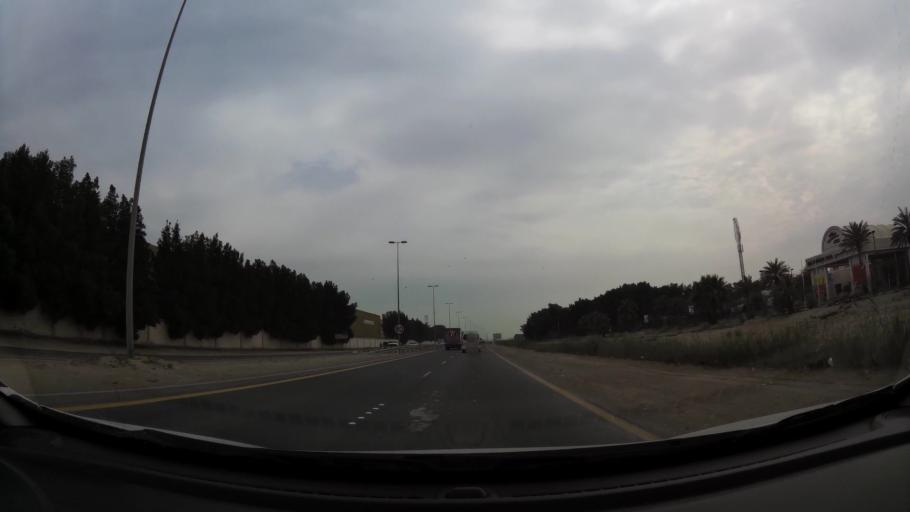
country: BH
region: Northern
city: Sitrah
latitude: 26.0841
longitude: 50.6123
